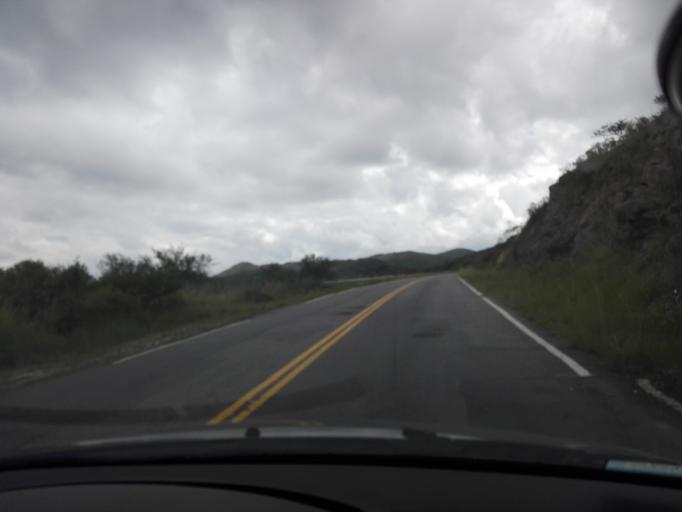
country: AR
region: Cordoba
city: Alta Gracia
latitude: -31.5931
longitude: -64.5208
